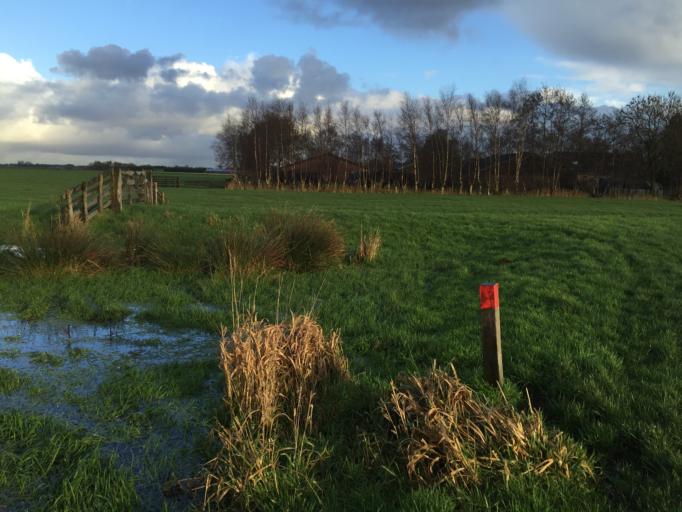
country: NL
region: South Holland
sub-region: Gemeente Nieuwkoop
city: Nieuwkoop
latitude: 52.1585
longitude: 4.7954
